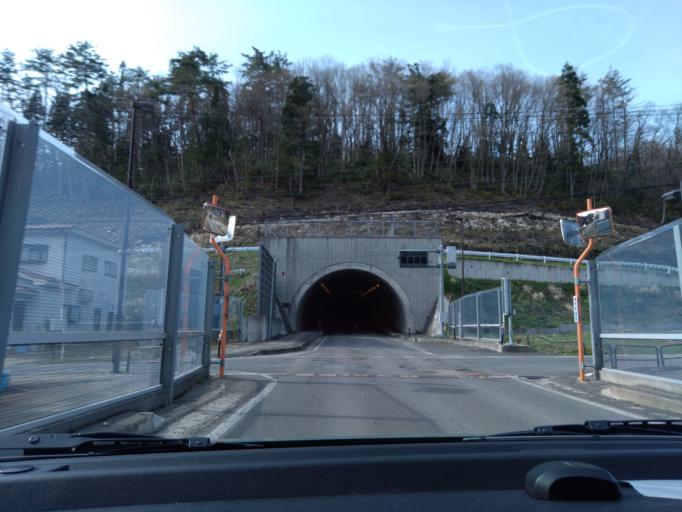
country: JP
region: Akita
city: Yokotemachi
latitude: 39.3191
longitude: 140.5770
